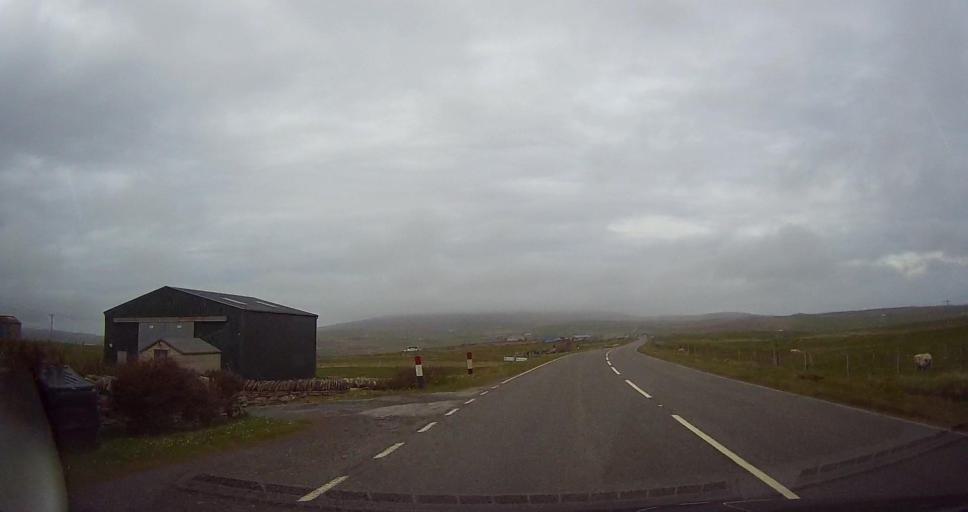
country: GB
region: Scotland
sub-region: Shetland Islands
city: Sandwick
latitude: 59.9127
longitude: -1.3019
